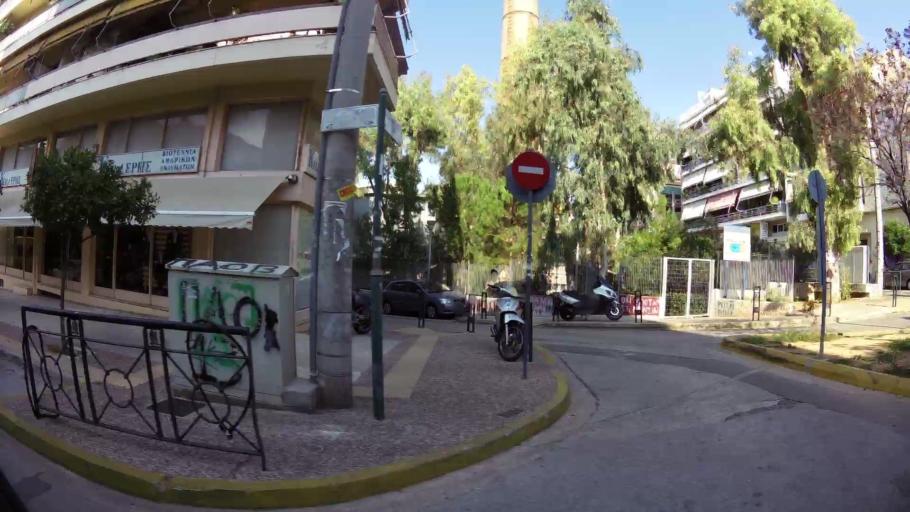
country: GR
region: Attica
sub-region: Nomarchia Athinas
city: Galatsi
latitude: 38.0152
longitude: 23.7501
